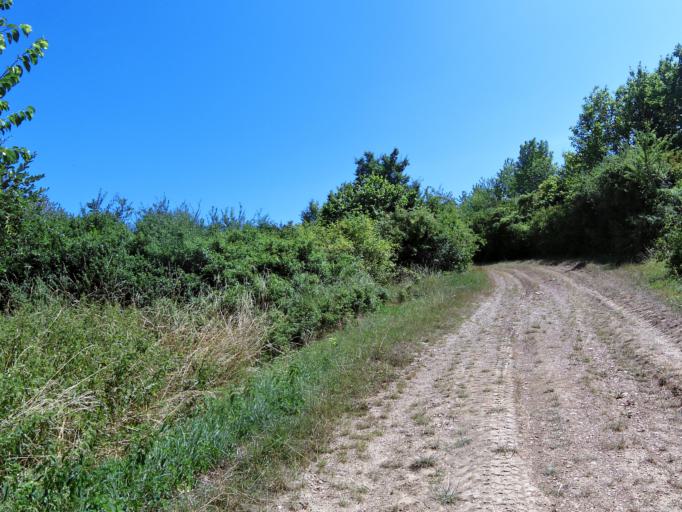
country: DE
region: Bavaria
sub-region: Regierungsbezirk Unterfranken
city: Gerbrunn
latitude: 49.7709
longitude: 10.0037
